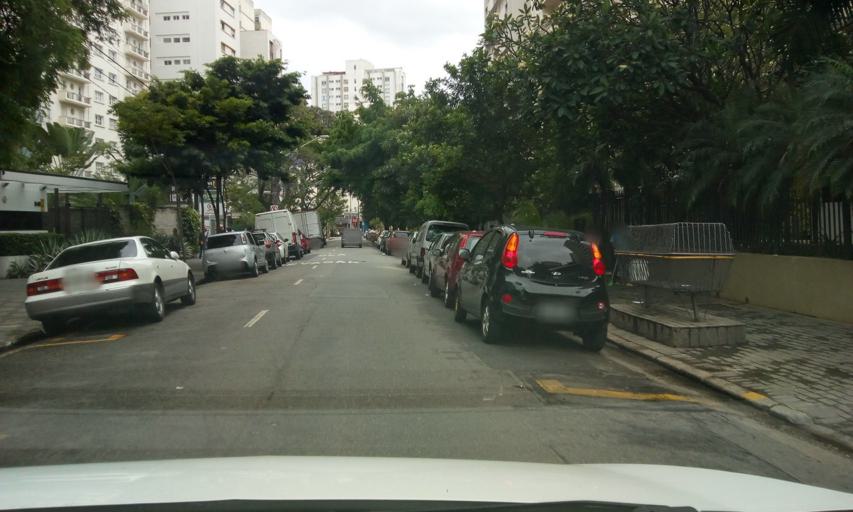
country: BR
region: Sao Paulo
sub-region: Sao Paulo
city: Sao Paulo
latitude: -23.5378
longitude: -46.6576
